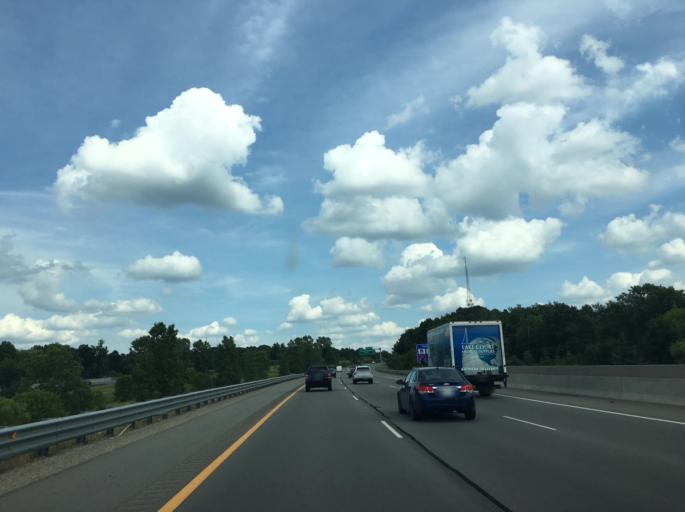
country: US
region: Michigan
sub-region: Oakland County
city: Clarkston
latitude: 42.7452
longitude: -83.3993
